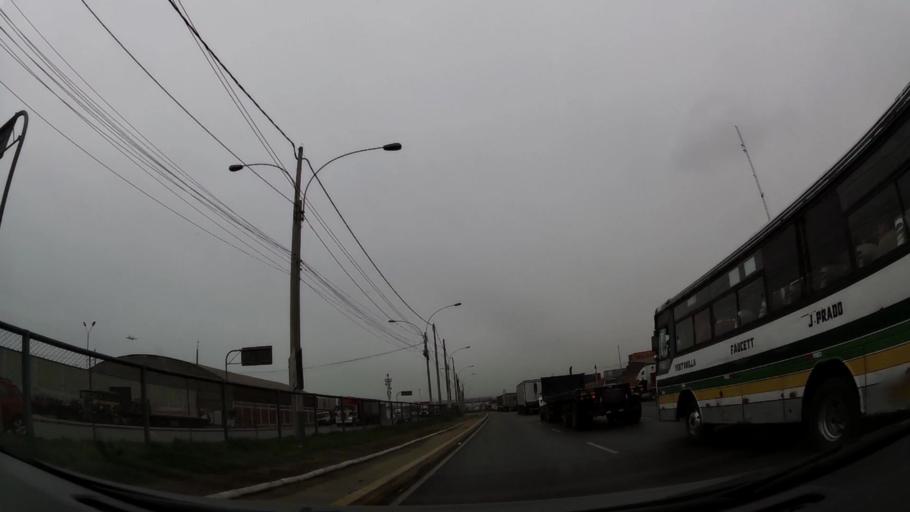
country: PE
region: Callao
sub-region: Callao
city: Callao
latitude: -11.9928
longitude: -77.1257
